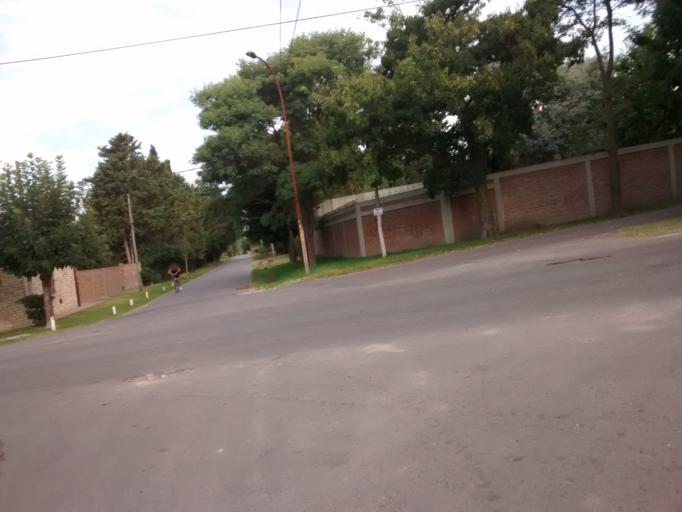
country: AR
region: Buenos Aires
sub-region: Partido de La Plata
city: La Plata
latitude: -34.8539
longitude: -58.0932
